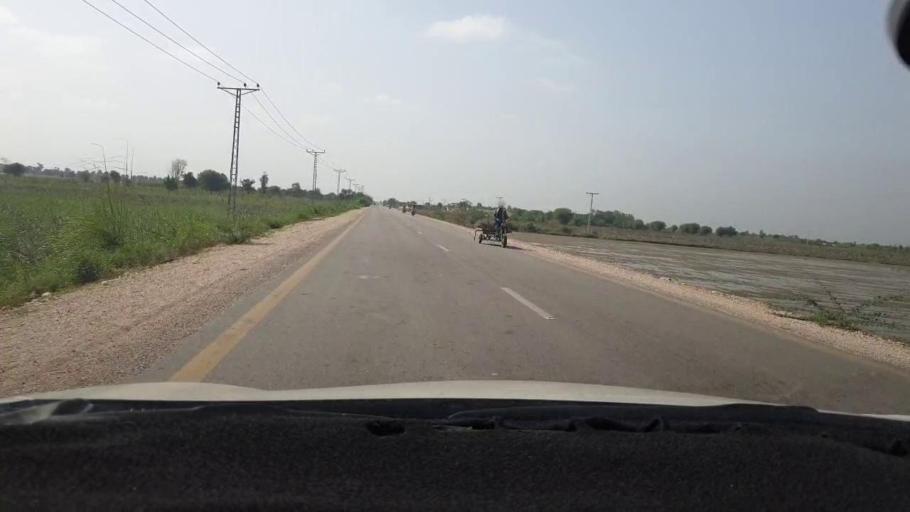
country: PK
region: Sindh
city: Tando Mittha Khan
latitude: 25.7799
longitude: 69.0713
